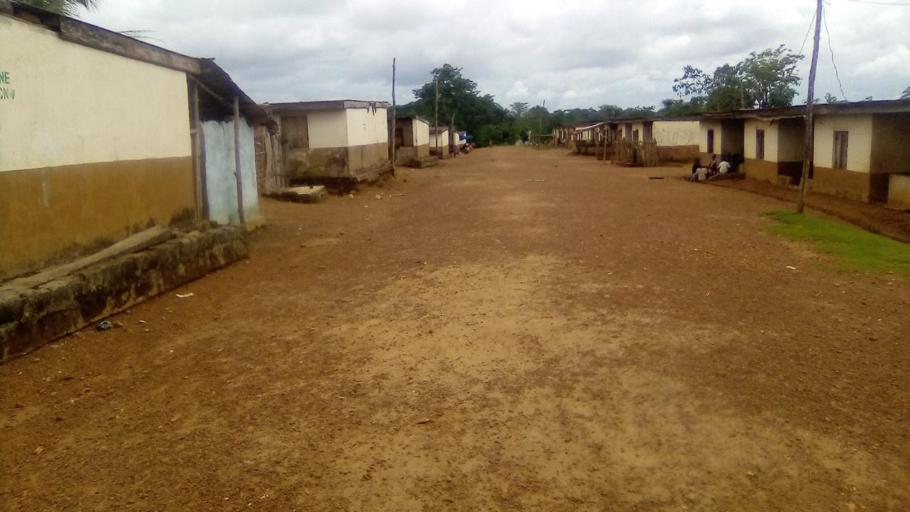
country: SL
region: Southern Province
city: Pujehun
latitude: 7.3713
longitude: -11.7265
